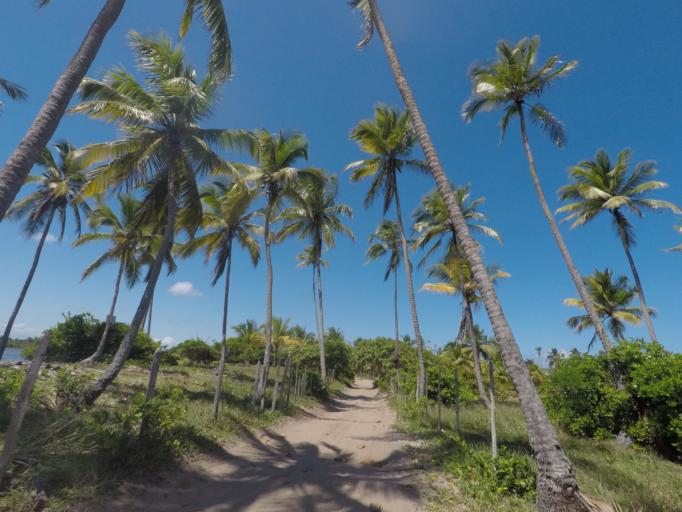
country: BR
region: Bahia
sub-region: Marau
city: Marau
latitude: -13.9992
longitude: -38.9449
